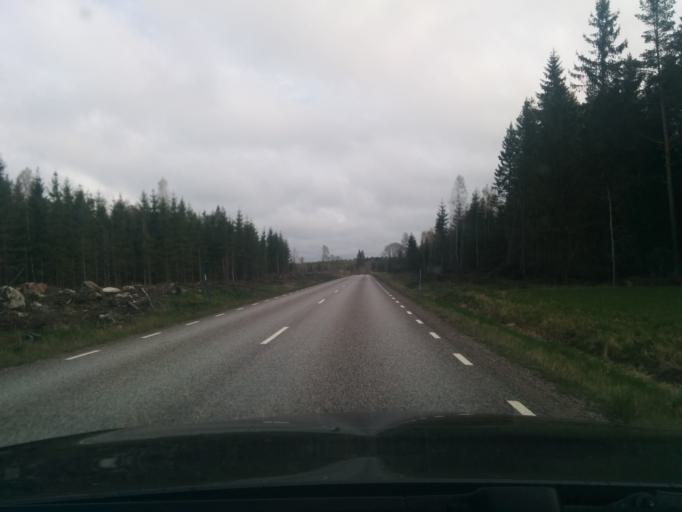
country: SE
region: Uppsala
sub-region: Tierps Kommun
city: Orbyhus
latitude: 60.2070
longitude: 17.6985
